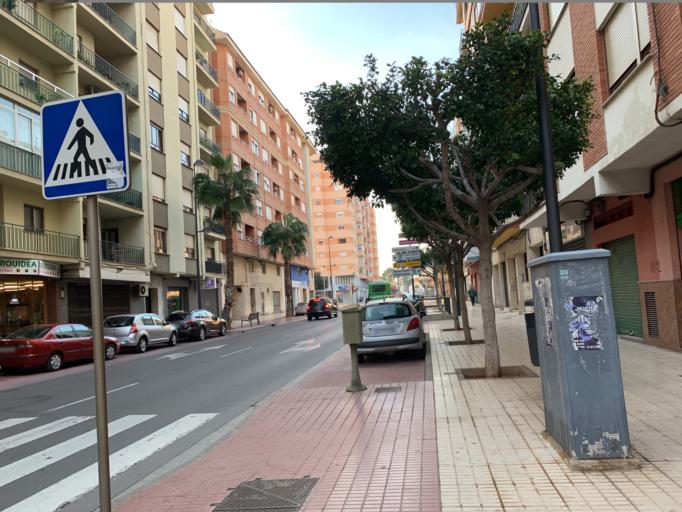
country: ES
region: Valencia
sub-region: Provincia de Castello
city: Castello de la Plana
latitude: 39.9909
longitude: -0.0484
